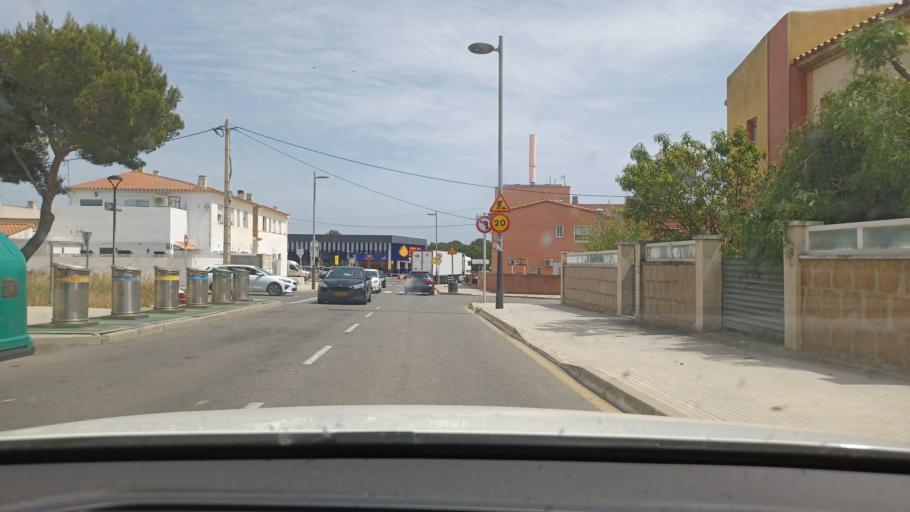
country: ES
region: Catalonia
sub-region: Provincia de Tarragona
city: Colldejou
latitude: 41.0011
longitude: 0.9288
